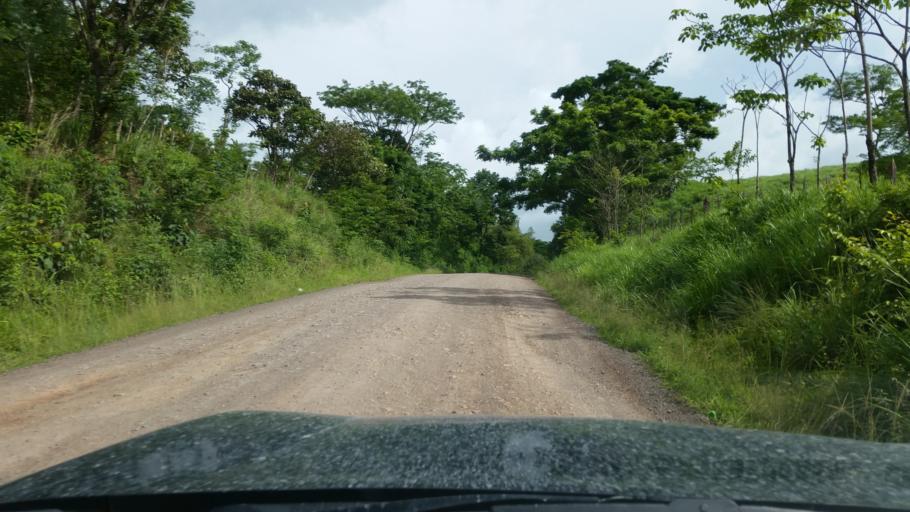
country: NI
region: Atlantico Norte (RAAN)
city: Siuna
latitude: 13.5853
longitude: -84.8133
